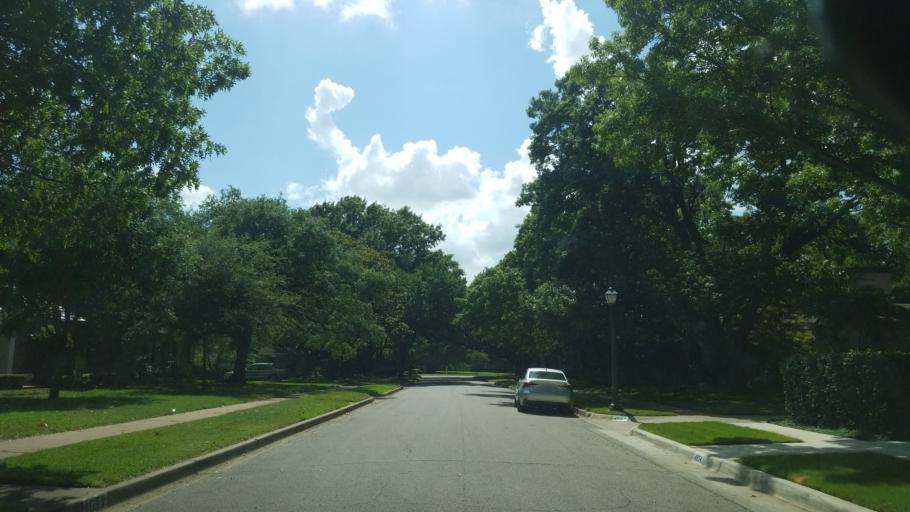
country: US
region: Texas
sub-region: Dallas County
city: Highland Park
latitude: 32.8295
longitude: -96.8179
